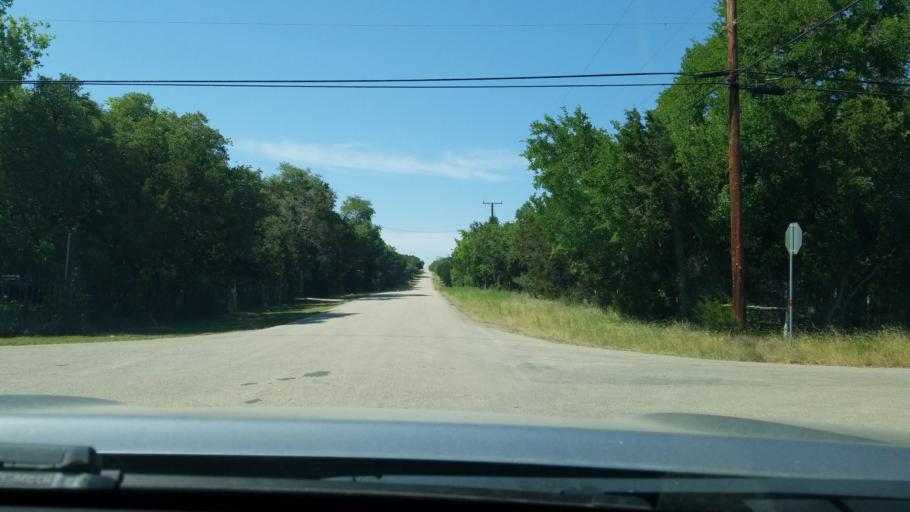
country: US
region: Texas
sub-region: Comal County
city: Bulverde
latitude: 29.7587
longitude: -98.5153
